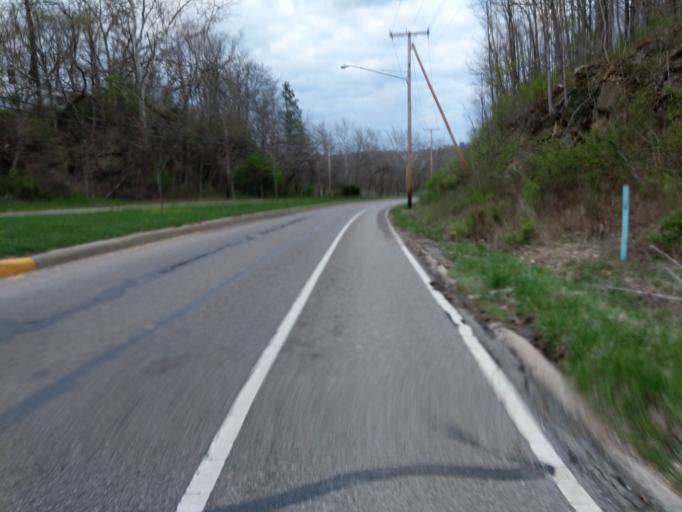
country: US
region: Ohio
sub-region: Athens County
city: Athens
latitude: 39.3397
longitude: -82.1035
